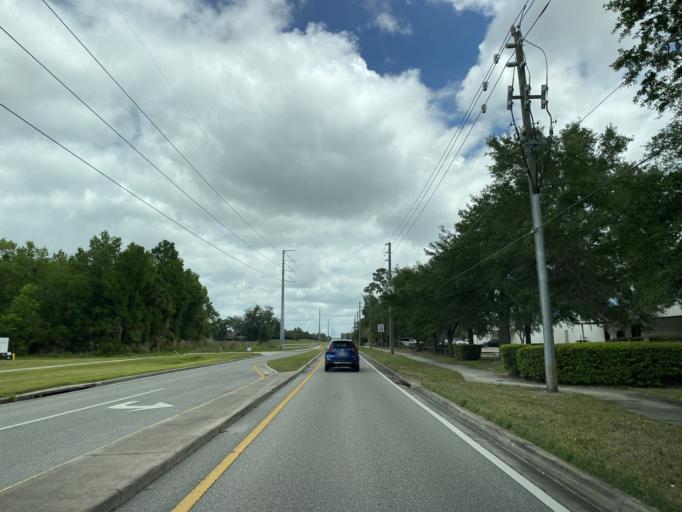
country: US
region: Florida
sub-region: Seminole County
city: Lake Mary
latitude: 28.8156
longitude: -81.3392
